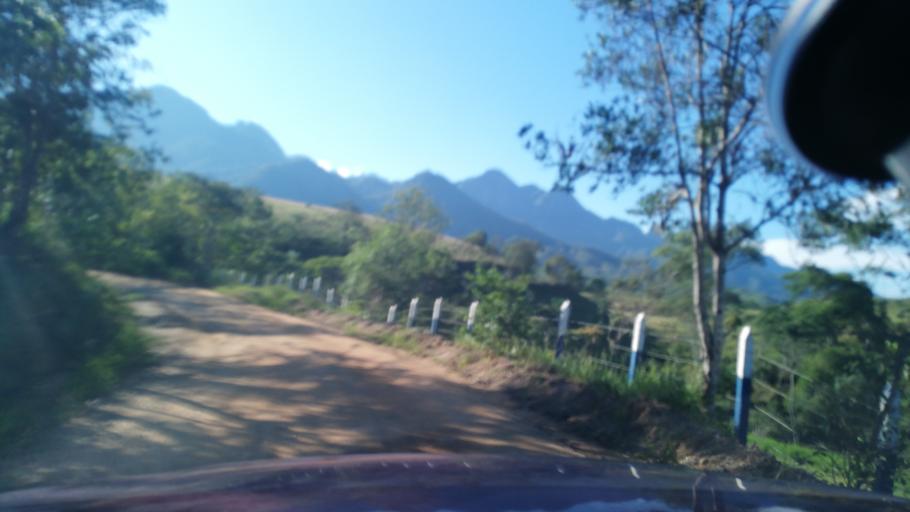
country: CO
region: Cundinamarca
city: Viani
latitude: 4.8266
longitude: -74.6180
